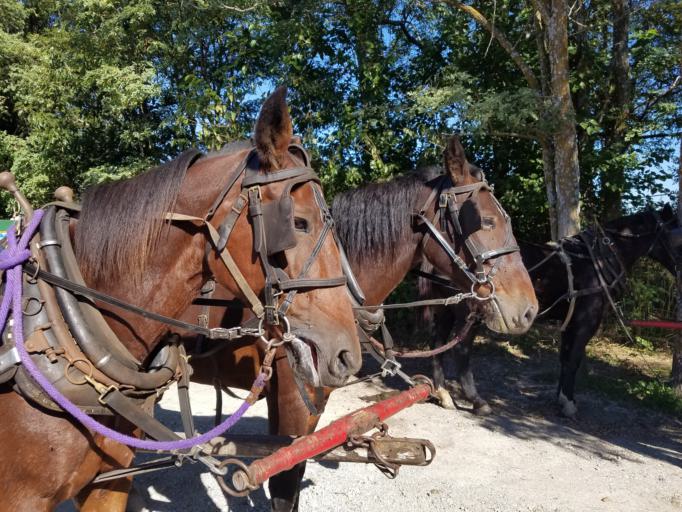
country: US
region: Iowa
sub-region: Decatur County
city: Lamoni
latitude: 40.6237
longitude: -93.8849
